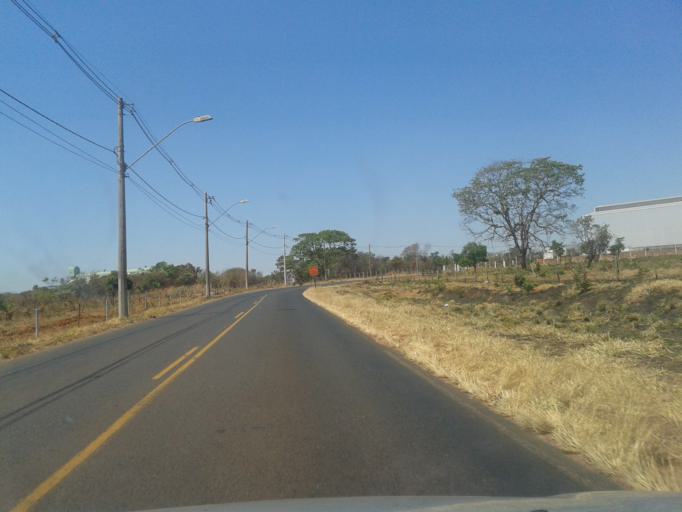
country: BR
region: Minas Gerais
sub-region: Uberlandia
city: Uberlandia
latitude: -18.8419
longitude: -48.3016
